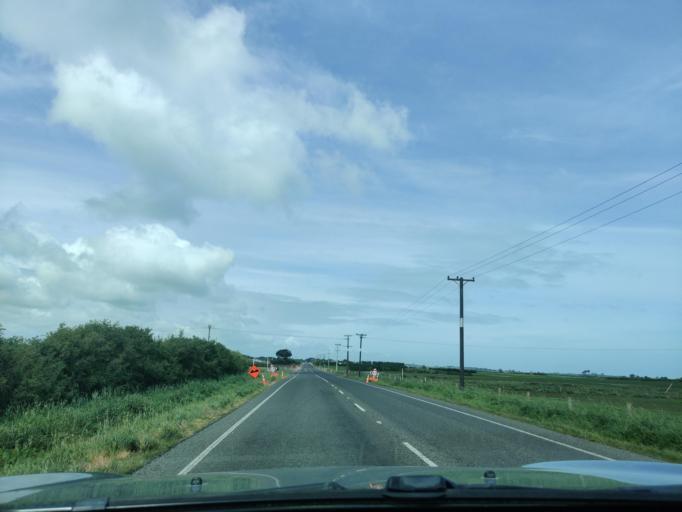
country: NZ
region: Taranaki
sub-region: South Taranaki District
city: Hawera
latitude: -39.5803
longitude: 174.2287
